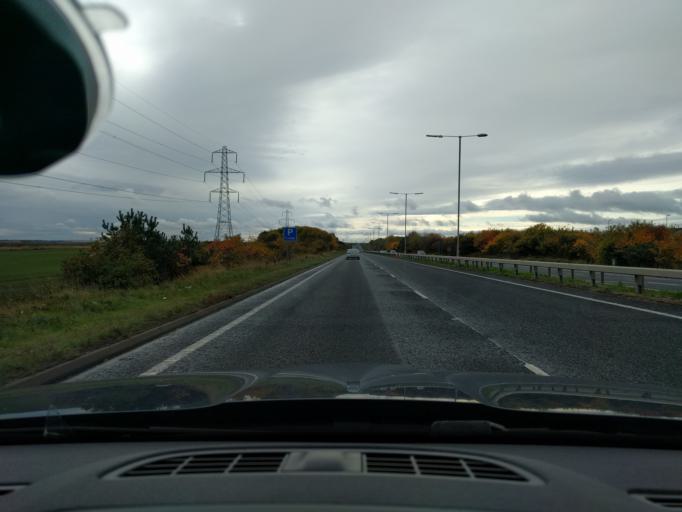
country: GB
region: England
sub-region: Northumberland
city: Newbiggin-by-the-Sea
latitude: 55.1678
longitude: -1.5342
